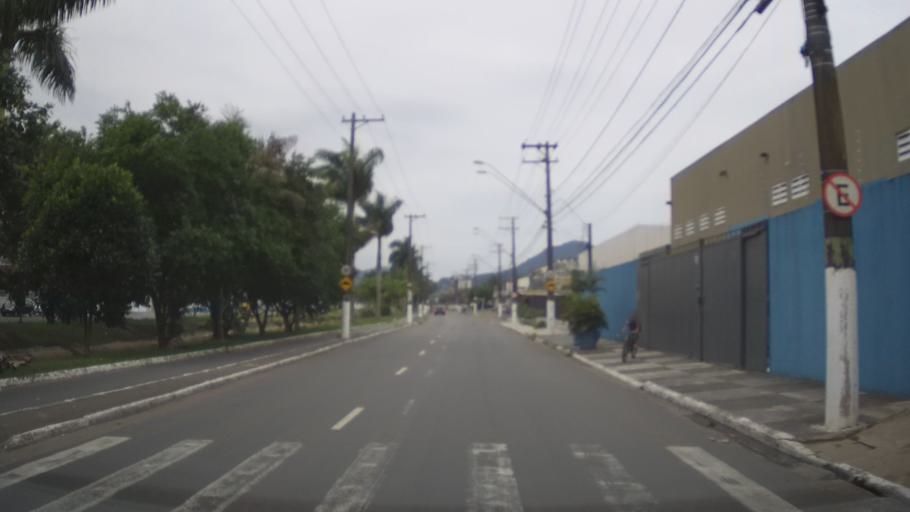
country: BR
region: Sao Paulo
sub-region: Praia Grande
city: Praia Grande
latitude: -24.0026
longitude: -46.4310
